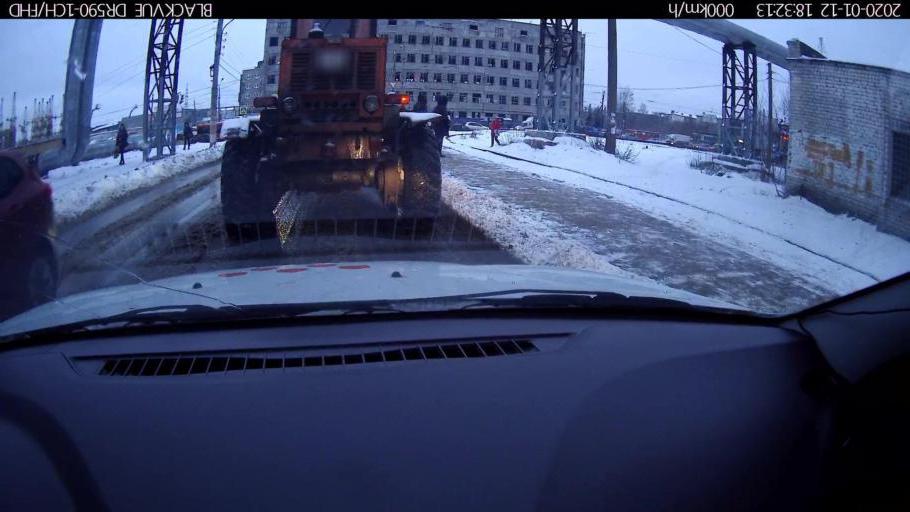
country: RU
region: Nizjnij Novgorod
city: Nizhniy Novgorod
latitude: 56.2654
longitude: 43.9228
